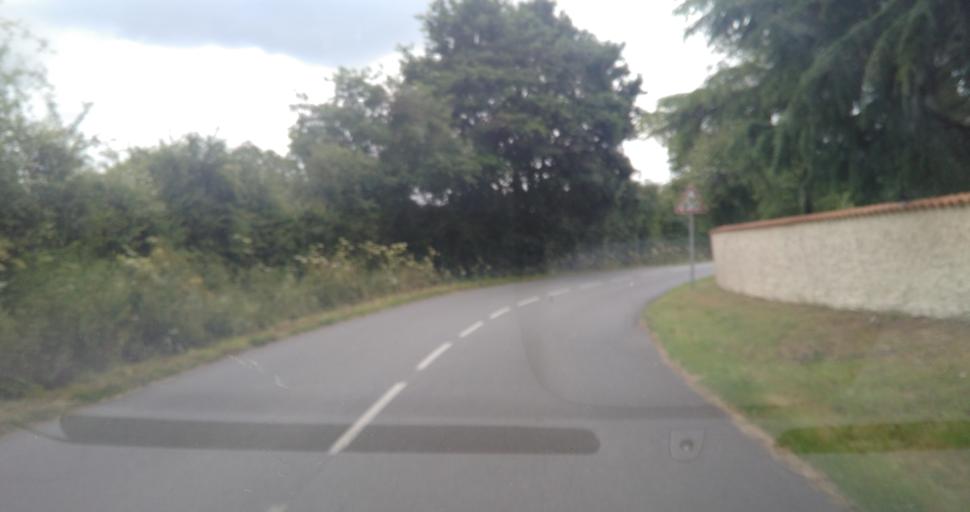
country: FR
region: Pays de la Loire
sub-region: Departement de la Vendee
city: La Chaize-le-Vicomte
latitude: 46.6771
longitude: -1.2964
